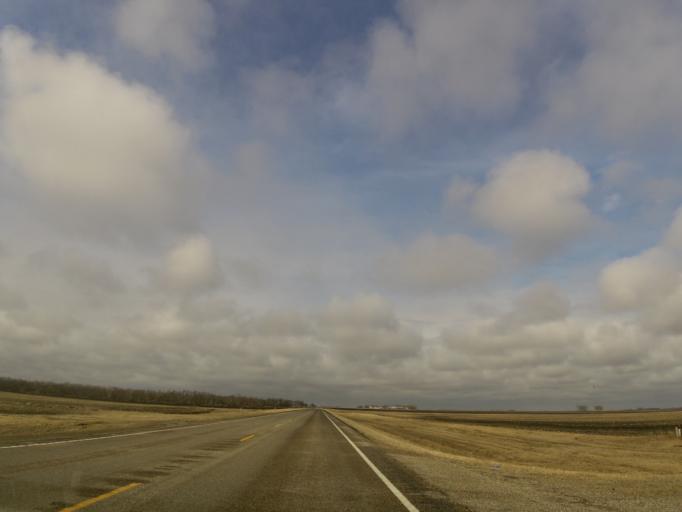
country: US
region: North Dakota
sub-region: Traill County
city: Hillsboro
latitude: 47.4978
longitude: -97.1510
